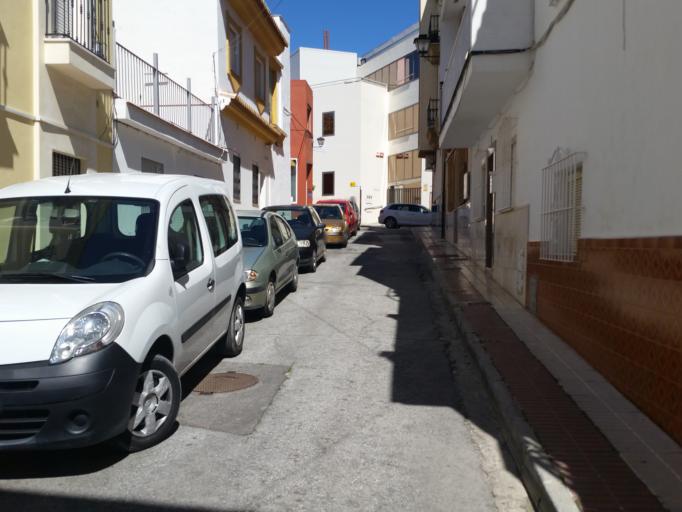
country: ES
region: Andalusia
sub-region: Provincia de Malaga
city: Benalmadena
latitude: 36.5974
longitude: -4.5337
